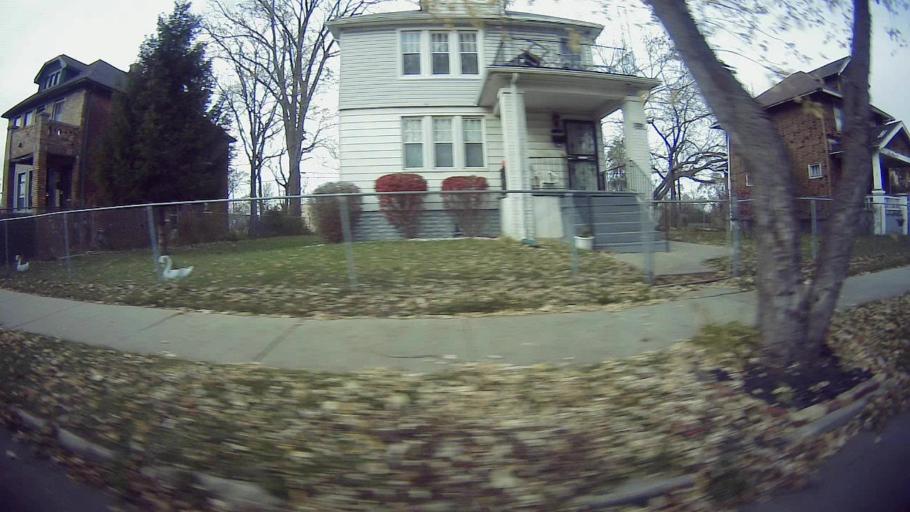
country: US
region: Michigan
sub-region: Wayne County
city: Highland Park
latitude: 42.3802
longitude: -83.1271
